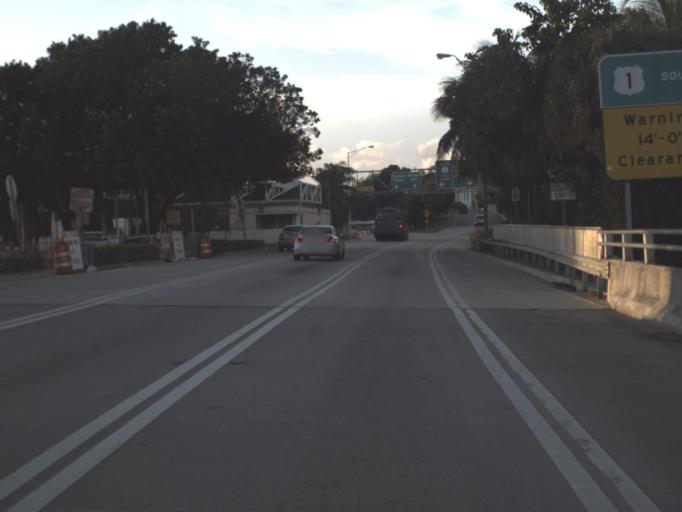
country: US
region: Florida
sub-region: Miami-Dade County
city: Miami
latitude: 25.7483
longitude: -80.2017
